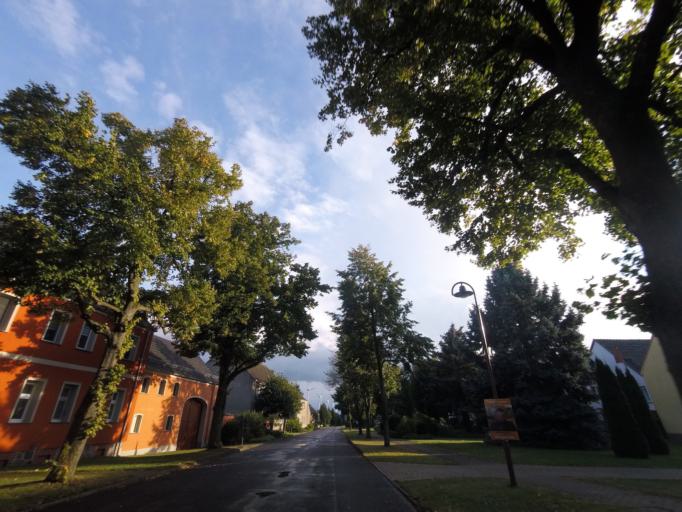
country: DE
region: Saxony-Anhalt
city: Kropstadt
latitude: 52.0108
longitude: 12.8194
